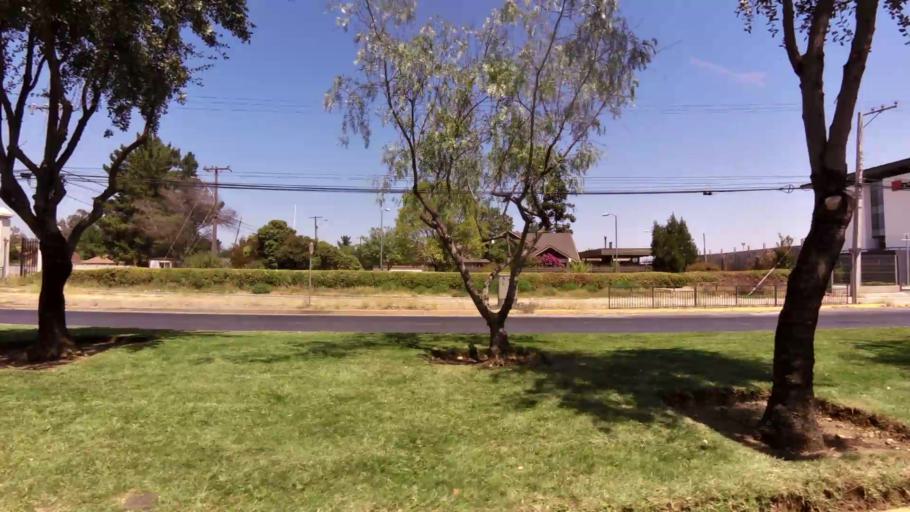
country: CL
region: Maule
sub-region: Provincia de Talca
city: Talca
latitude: -35.4366
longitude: -71.6219
